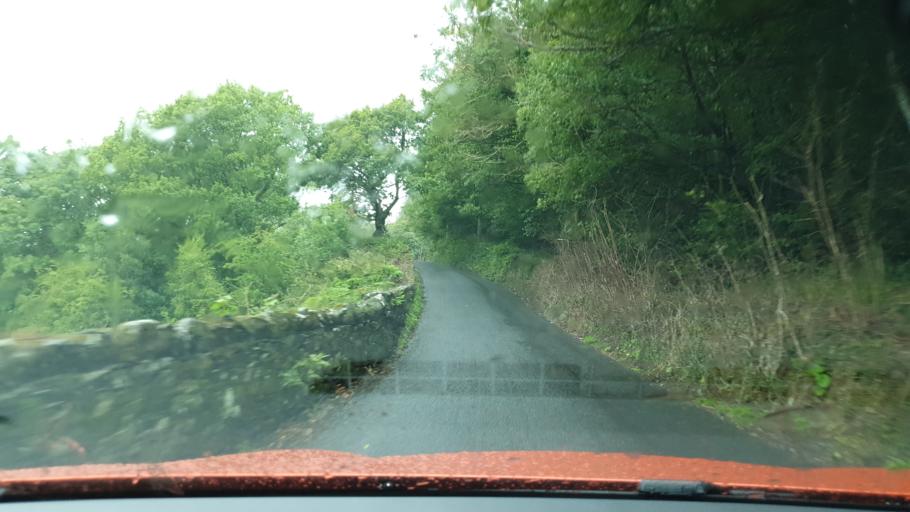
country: GB
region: England
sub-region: Cumbria
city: Millom
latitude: 54.2874
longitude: -3.2325
